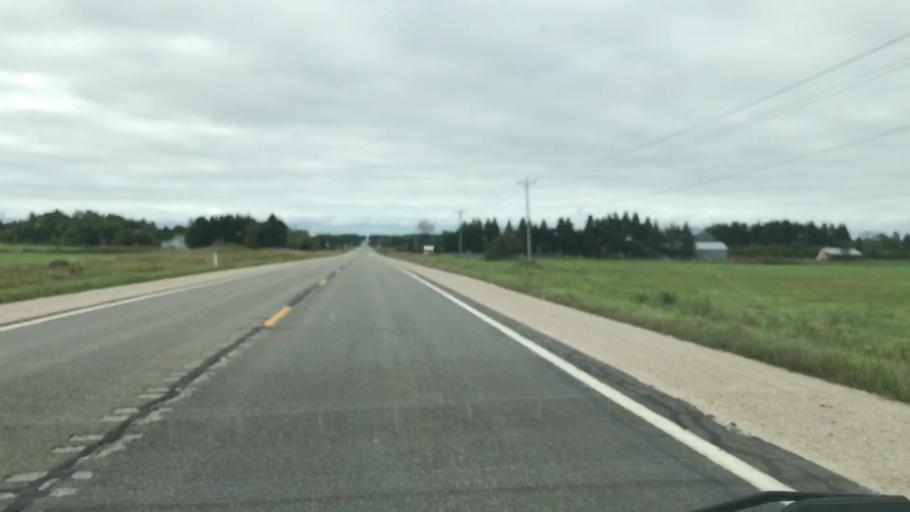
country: US
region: Michigan
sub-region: Luce County
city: Newberry
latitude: 46.1528
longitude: -85.5715
